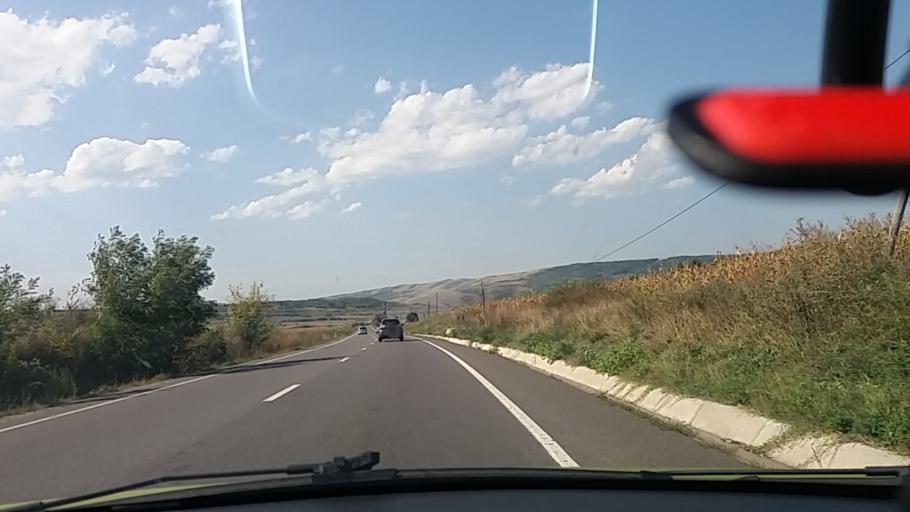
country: RO
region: Sibiu
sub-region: Comuna Seica Mare
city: Seica Mare
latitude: 45.9696
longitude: 24.1541
